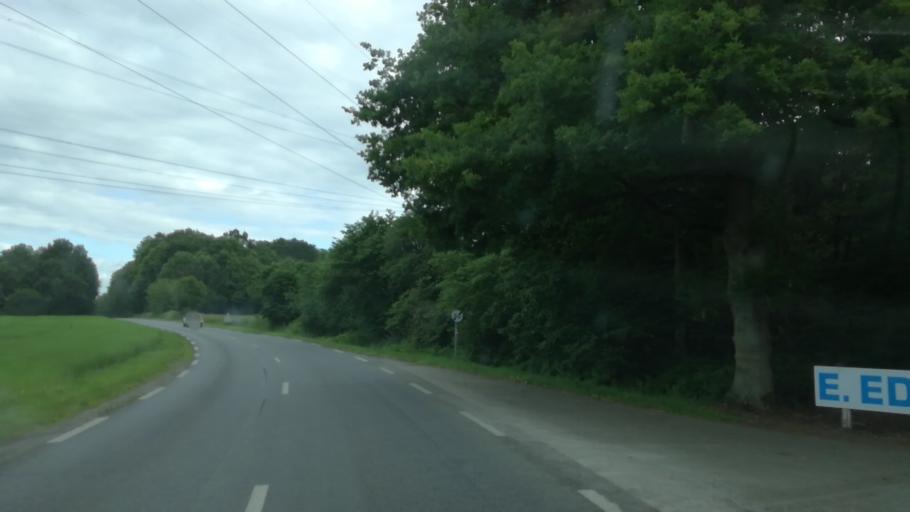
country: FR
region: Haute-Normandie
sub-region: Departement de l'Eure
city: Le Neubourg
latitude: 49.2072
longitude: 0.8521
